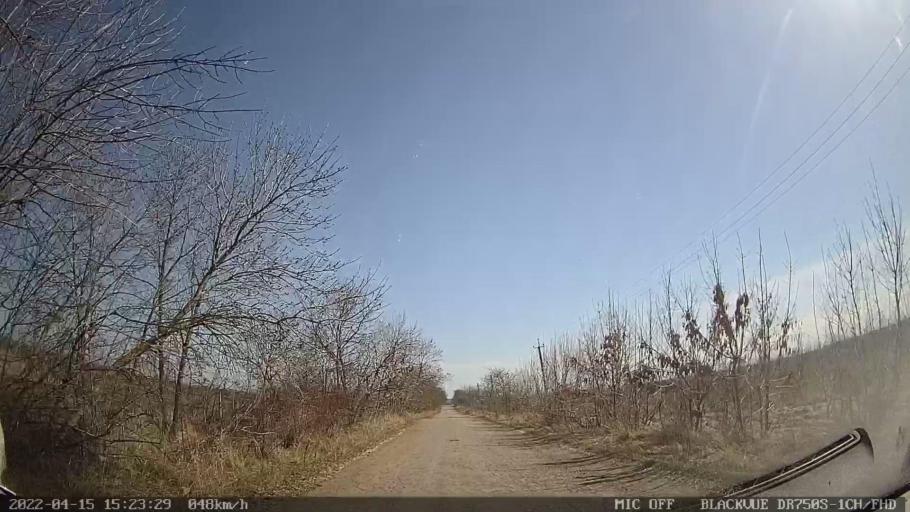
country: MD
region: Raionul Ocnita
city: Otaci
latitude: 48.3746
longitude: 27.9195
